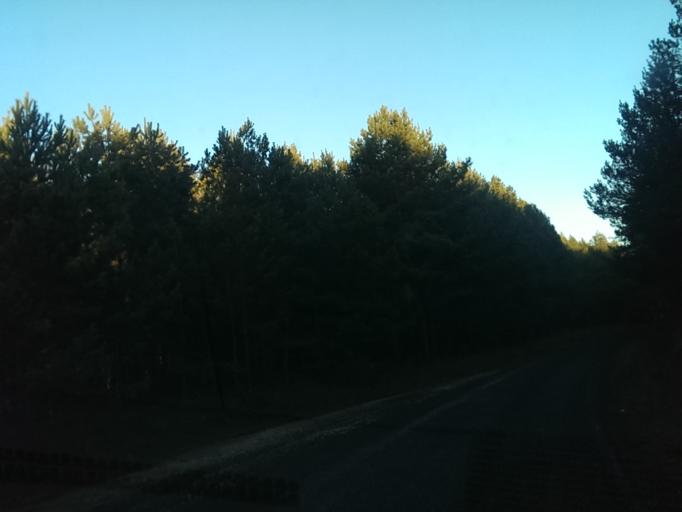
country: PL
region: Kujawsko-Pomorskie
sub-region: Powiat nakielski
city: Naklo nad Notecia
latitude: 53.0481
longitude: 17.6395
